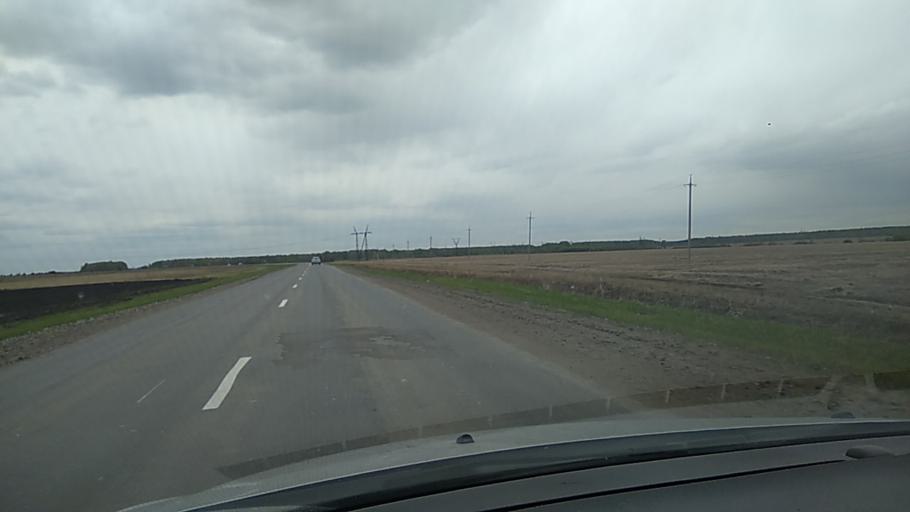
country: RU
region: Sverdlovsk
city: Martyush
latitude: 56.4104
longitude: 61.8021
